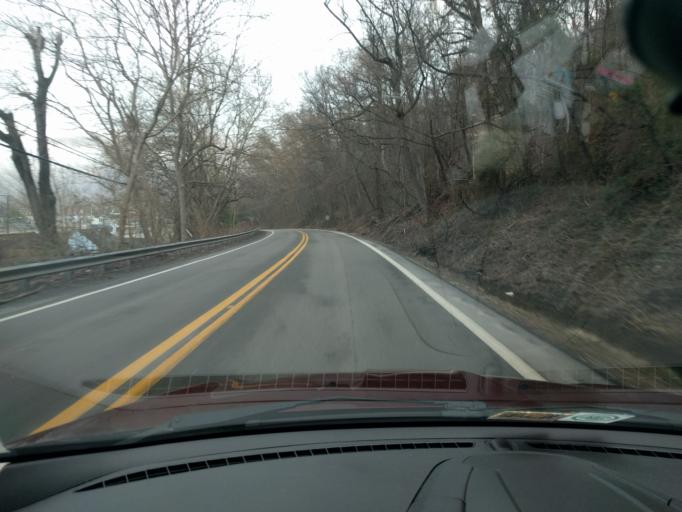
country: US
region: West Virginia
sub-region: Kanawha County
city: Montgomery
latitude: 38.1693
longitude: -81.3029
